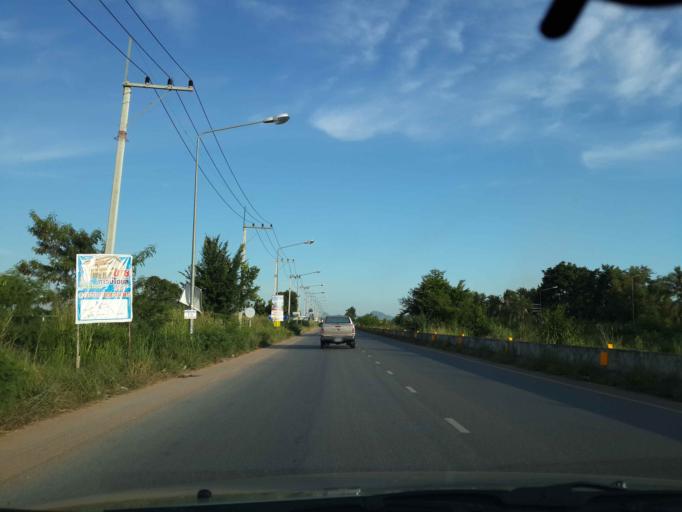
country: TH
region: Chon Buri
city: Phatthaya
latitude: 12.8779
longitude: 100.9065
